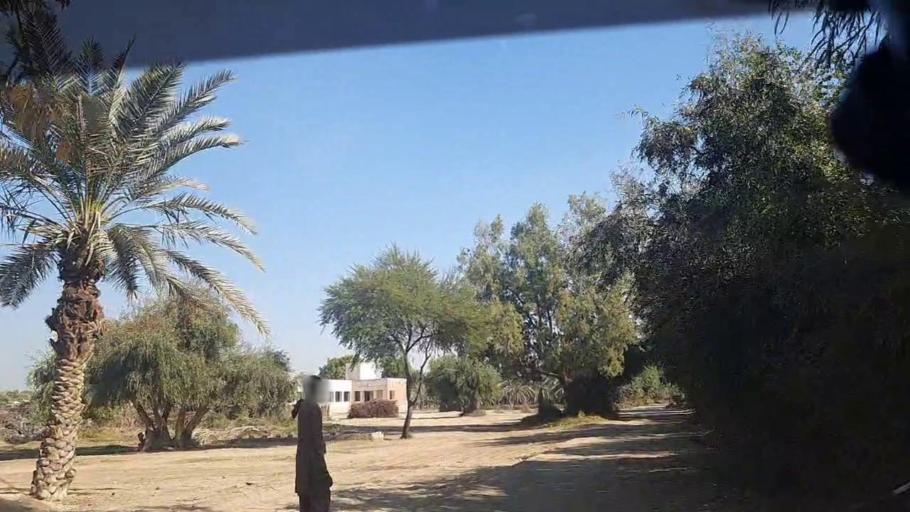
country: PK
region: Sindh
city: Khanpur
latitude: 27.6607
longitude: 69.2792
